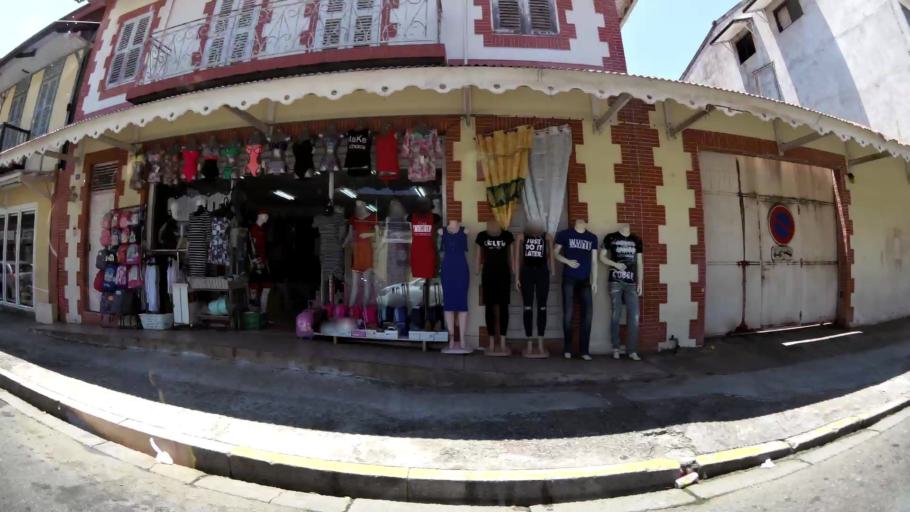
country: GF
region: Guyane
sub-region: Guyane
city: Cayenne
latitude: 4.9375
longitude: -52.3320
